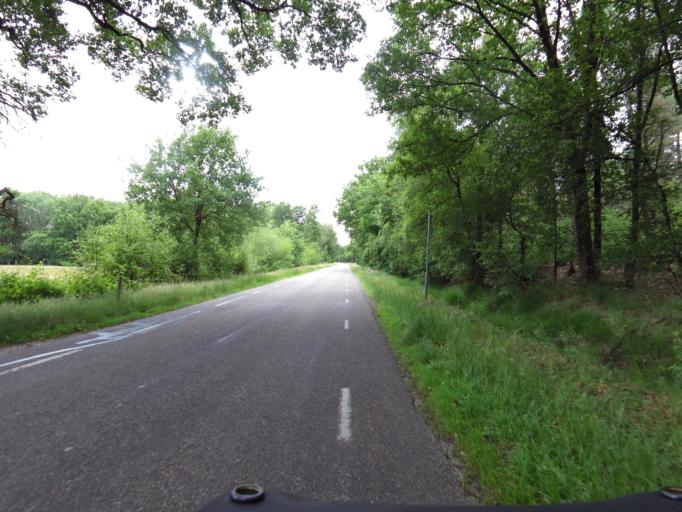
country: NL
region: North Brabant
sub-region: Gemeente Oirschot
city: Middelbeers
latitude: 51.4345
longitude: 5.2099
